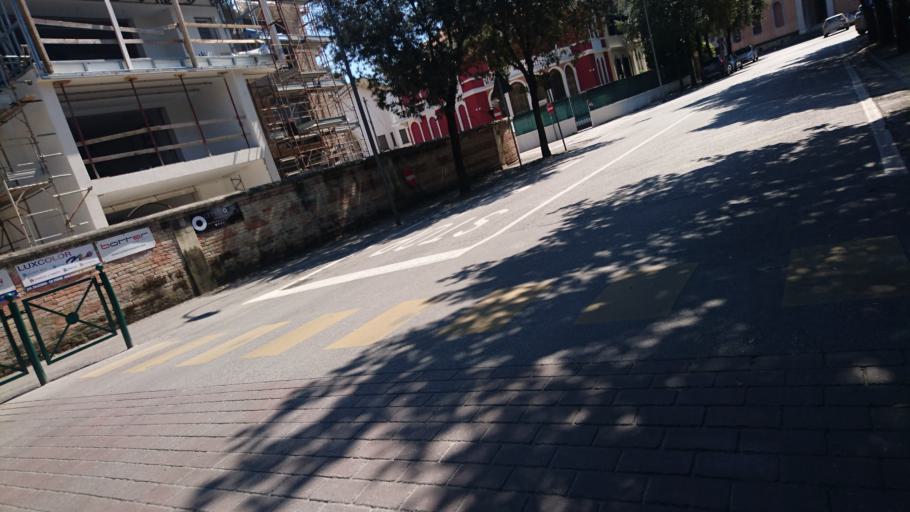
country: IT
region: Veneto
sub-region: Provincia di Treviso
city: Treviso
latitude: 45.6642
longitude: 12.2378
